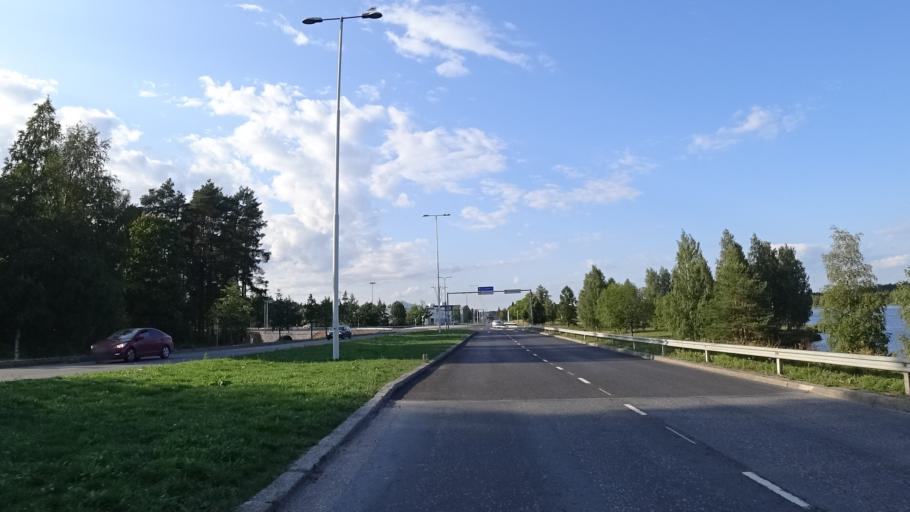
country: FI
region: South Karelia
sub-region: Imatra
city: Imatra
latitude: 61.1875
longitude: 28.7778
